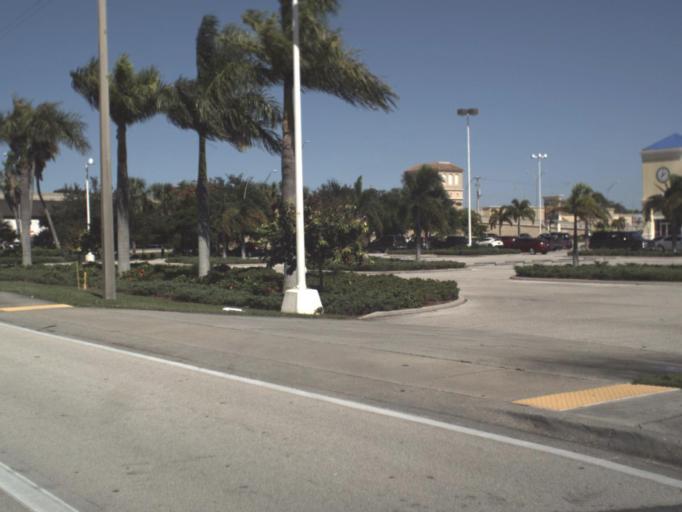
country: US
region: Florida
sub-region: Lee County
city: Pine Manor
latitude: 26.5956
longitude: -81.8718
